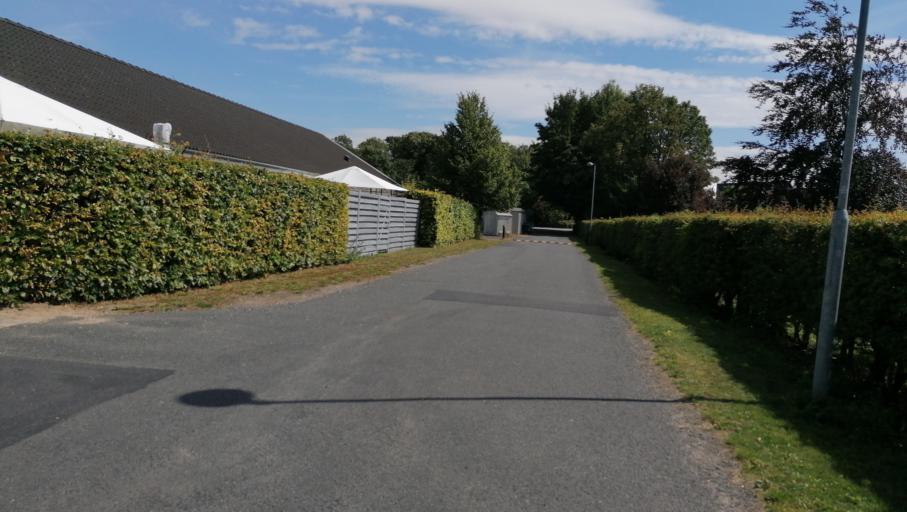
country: DK
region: Zealand
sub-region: Odsherred Kommune
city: Horve
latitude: 55.7894
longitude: 11.4677
